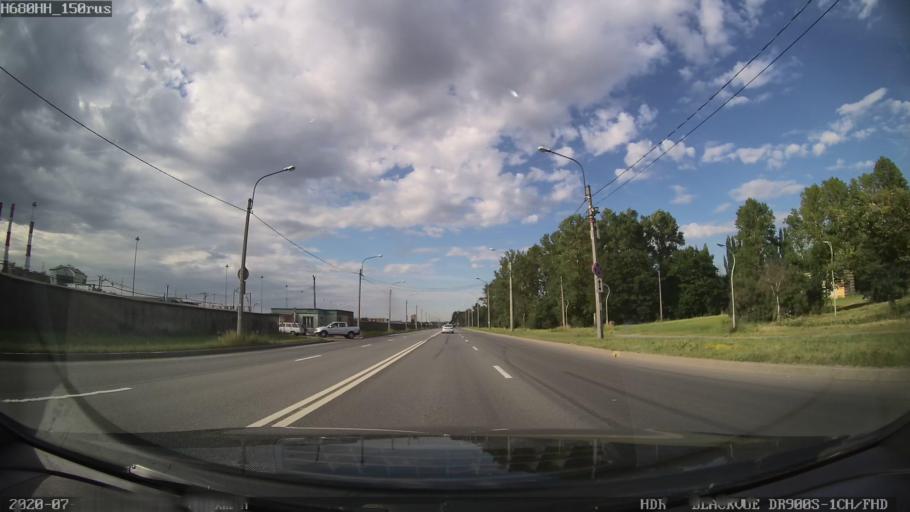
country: RU
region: St.-Petersburg
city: Avtovo
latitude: 59.8672
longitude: 30.2962
